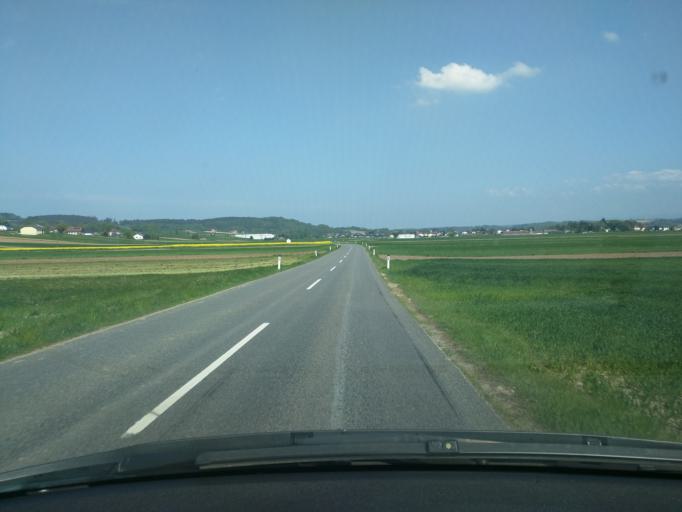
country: AT
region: Lower Austria
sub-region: Politischer Bezirk Amstetten
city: Sankt Georgen am Ybbsfelde
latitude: 48.1302
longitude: 14.9636
